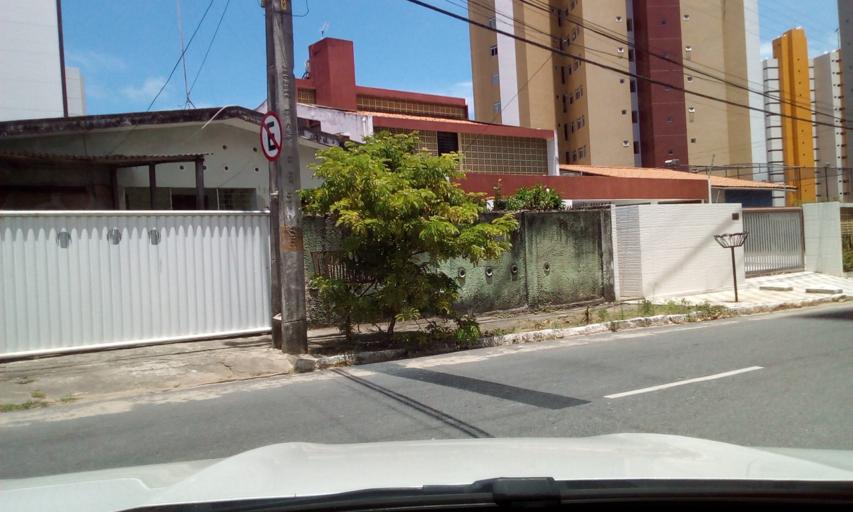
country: BR
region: Paraiba
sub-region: Joao Pessoa
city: Joao Pessoa
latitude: -7.1225
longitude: -34.8330
